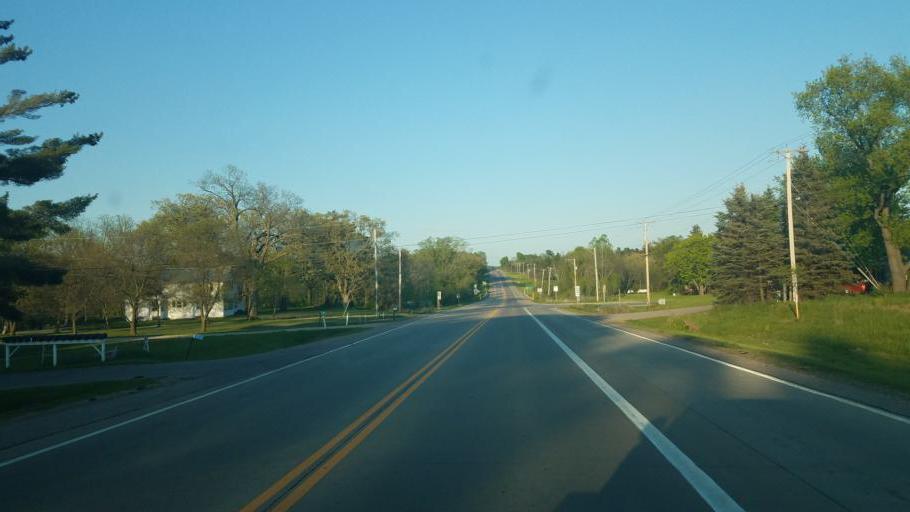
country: US
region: Wisconsin
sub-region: Sauk County
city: Reedsburg
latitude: 43.5326
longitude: -89.9563
